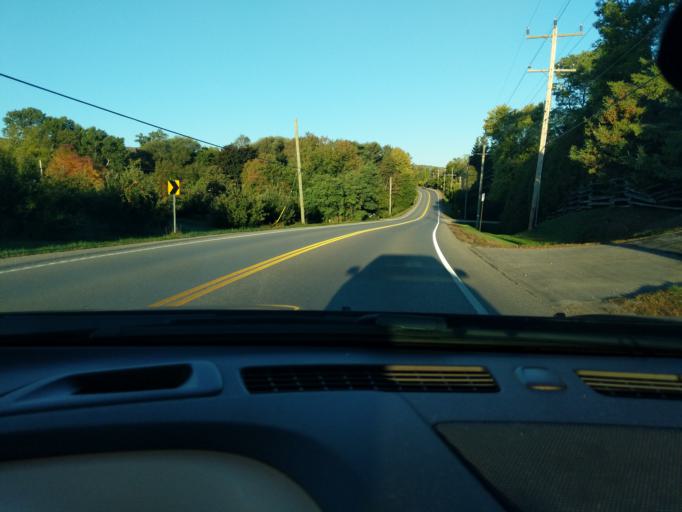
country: CA
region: Ontario
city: Collingwood
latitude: 44.4984
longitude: -80.2754
